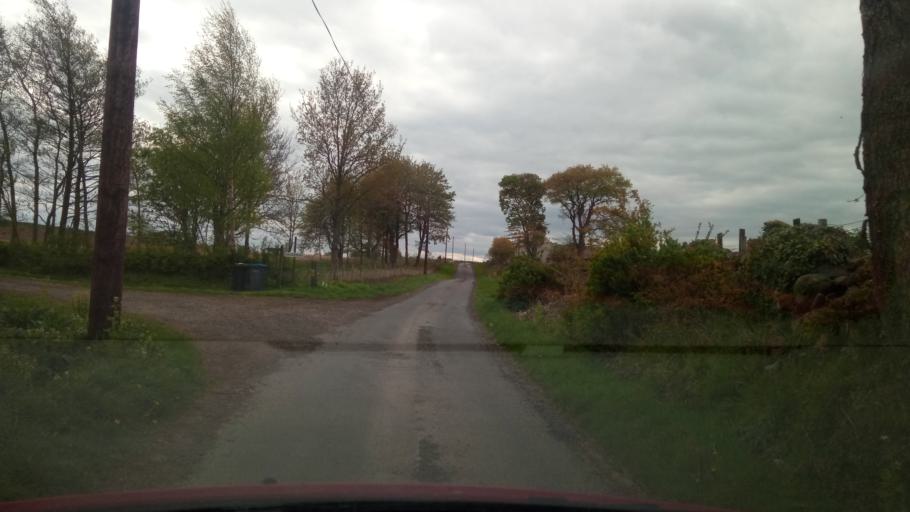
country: GB
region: Scotland
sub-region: The Scottish Borders
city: Jedburgh
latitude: 55.5128
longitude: -2.6076
